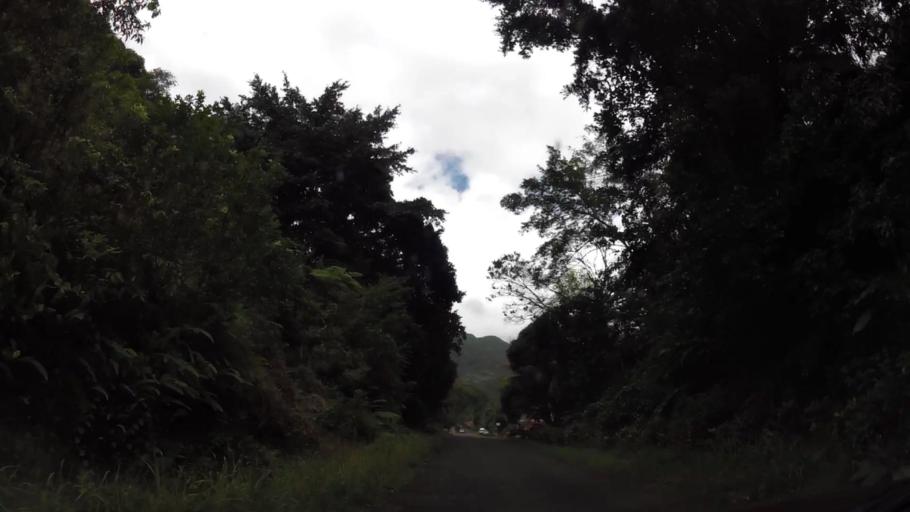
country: DM
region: Saint David
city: Castle Bruce
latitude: 15.4409
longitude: -61.2601
